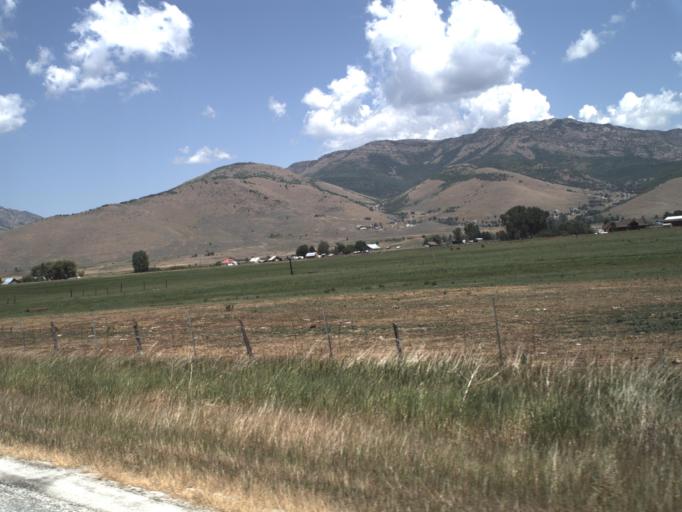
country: US
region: Utah
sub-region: Weber County
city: Wolf Creek
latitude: 41.2533
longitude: -111.7612
